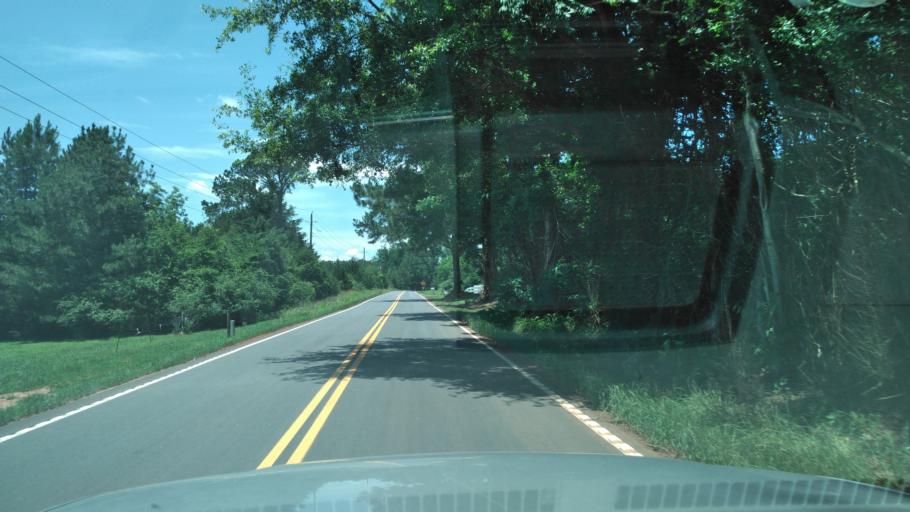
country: US
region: South Carolina
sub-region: Greenwood County
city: Ware Shoals
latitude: 34.4047
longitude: -82.1254
